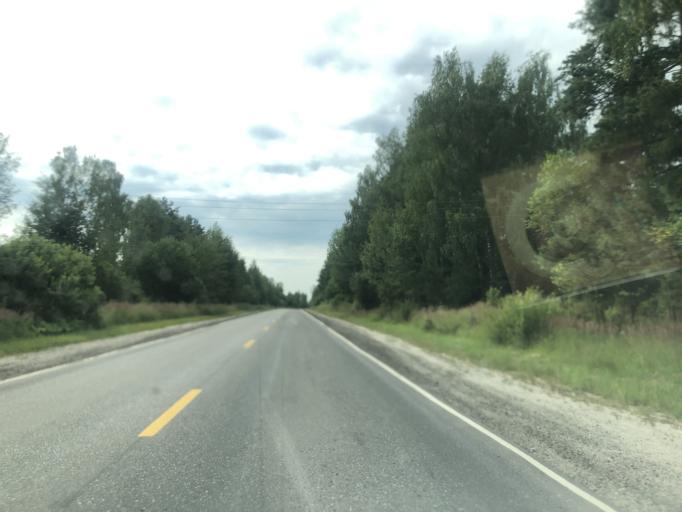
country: RU
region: Ivanovo
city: Pestyaki
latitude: 56.7266
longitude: 42.6028
